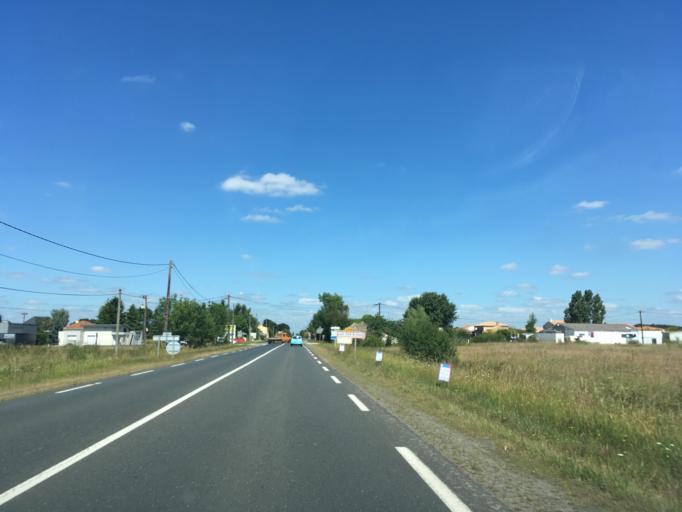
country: FR
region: Pays de la Loire
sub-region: Departement de la Loire-Atlantique
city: Les Sorinieres
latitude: 47.1395
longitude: -1.5200
